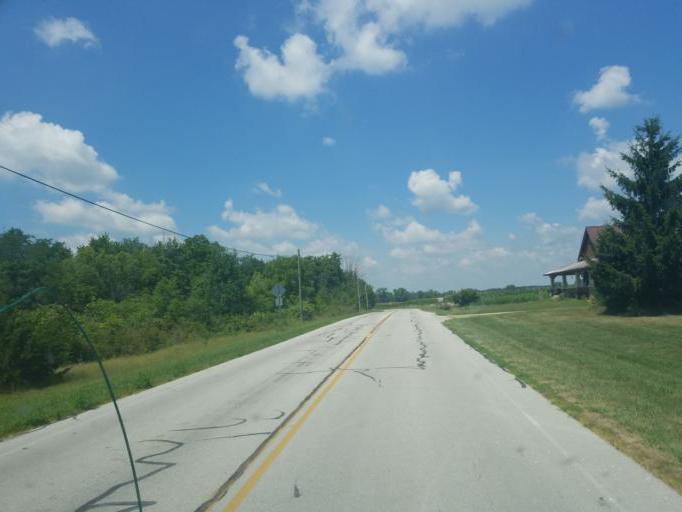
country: US
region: Ohio
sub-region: Mercer County
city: Rockford
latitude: 40.6775
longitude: -84.5094
